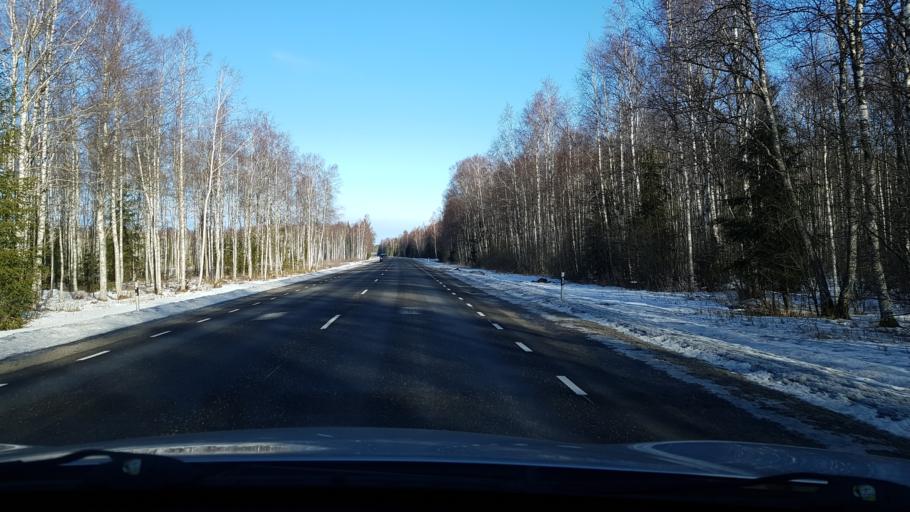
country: EE
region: Viljandimaa
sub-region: Vohma linn
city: Vohma
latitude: 58.5989
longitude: 25.5726
